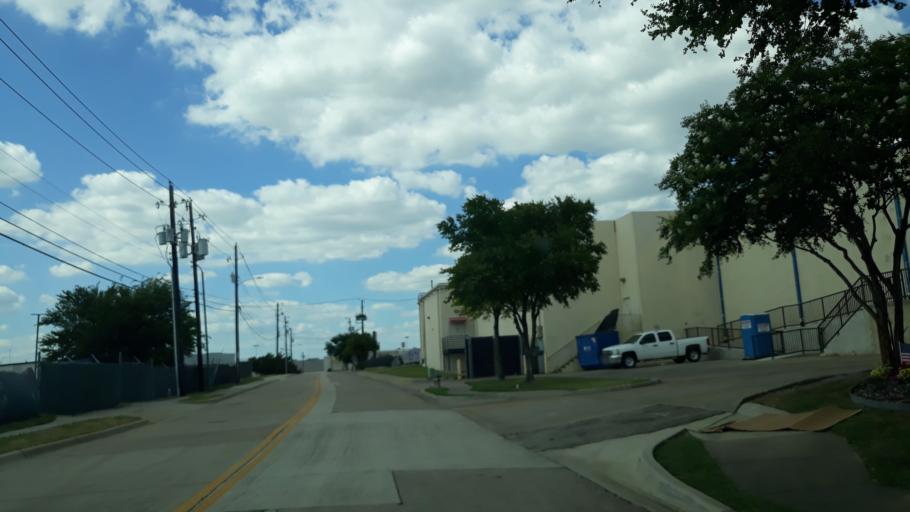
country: US
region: Texas
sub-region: Dallas County
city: Irving
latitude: 32.8342
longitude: -96.9980
